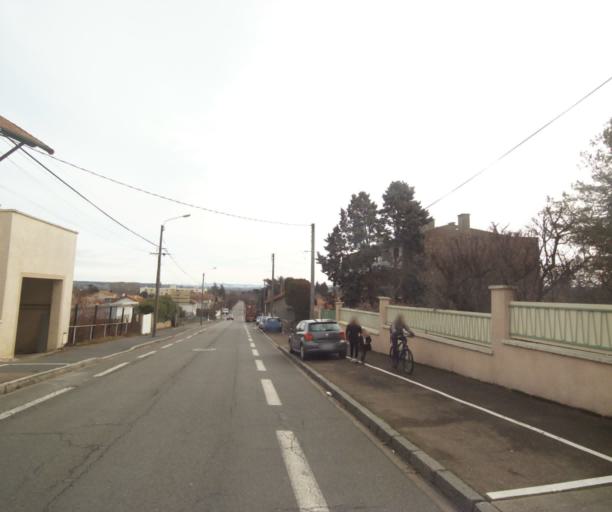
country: FR
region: Rhone-Alpes
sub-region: Departement de la Loire
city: Roanne
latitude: 46.0243
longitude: 4.0585
